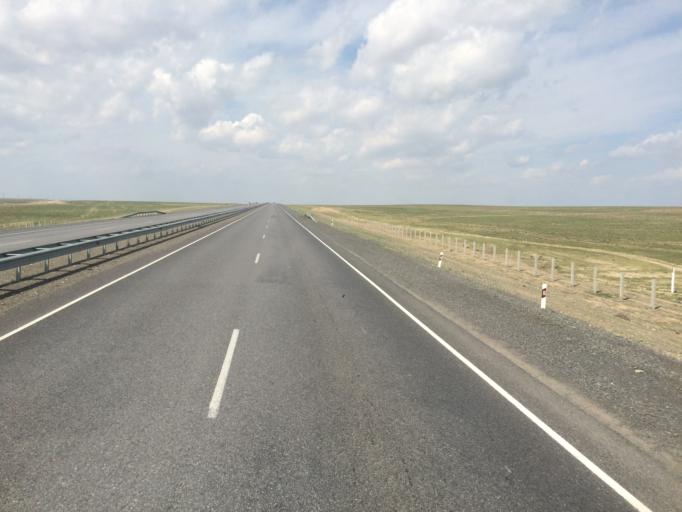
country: KZ
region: Qyzylorda
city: Shalqiya
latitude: 43.8591
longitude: 67.4007
